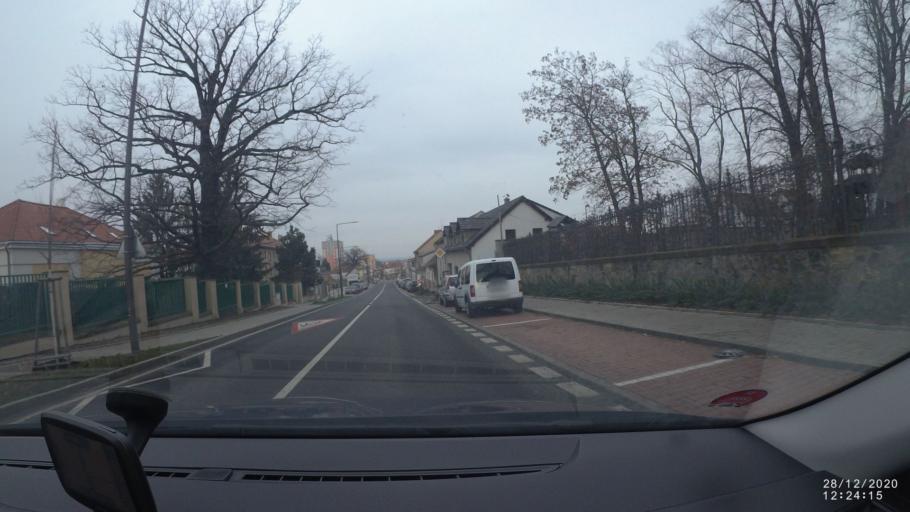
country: CZ
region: Central Bohemia
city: Brandys nad Labem-Stara Boleslav
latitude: 50.1810
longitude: 14.6564
